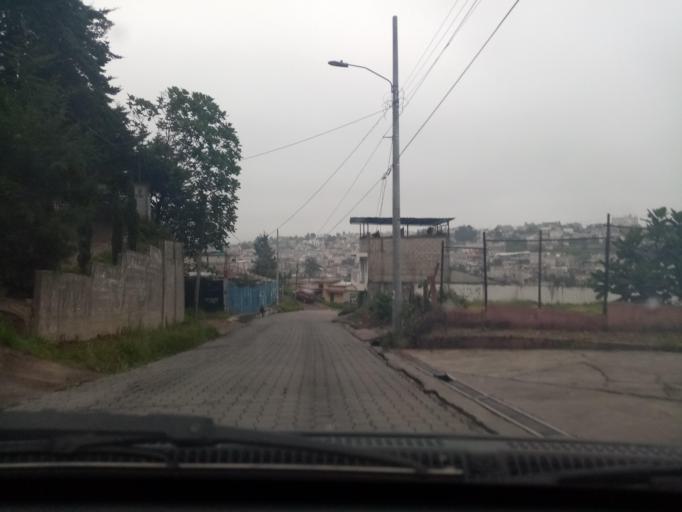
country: GT
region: Quetzaltenango
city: Quetzaltenango
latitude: 14.8478
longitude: -91.5138
